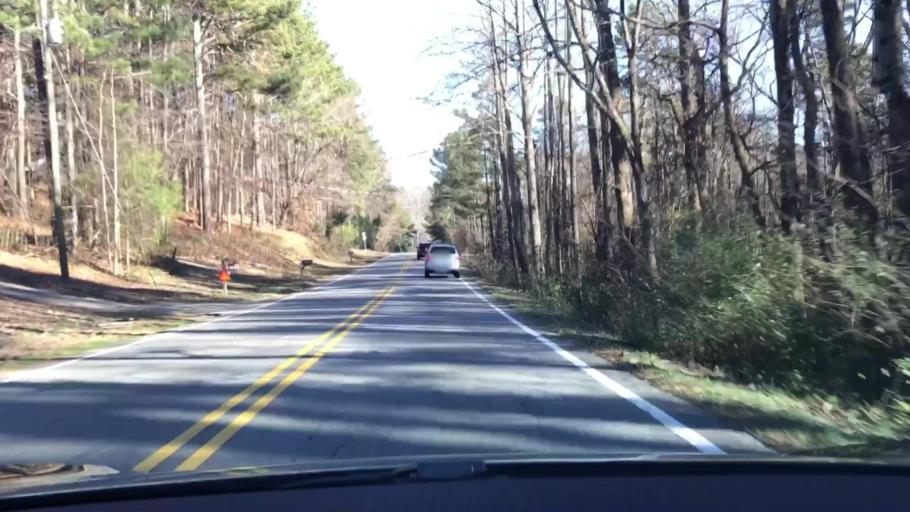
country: US
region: Georgia
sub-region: Forsyth County
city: Cumming
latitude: 34.1869
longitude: -84.1191
